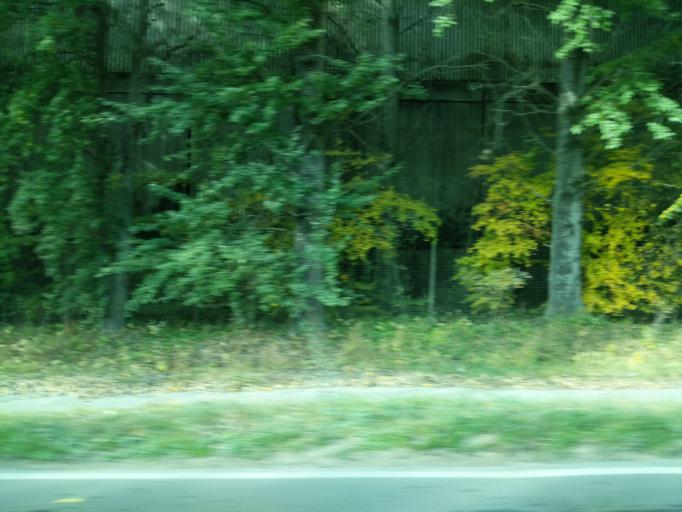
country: DE
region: Schleswig-Holstein
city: Lagerdorf
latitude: 53.8770
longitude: 9.5881
